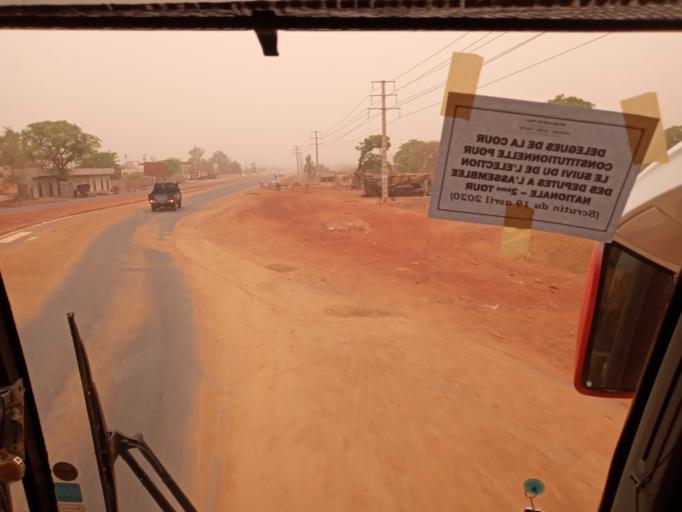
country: ML
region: Koulikoro
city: Koulikoro
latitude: 12.8263
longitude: -7.6230
